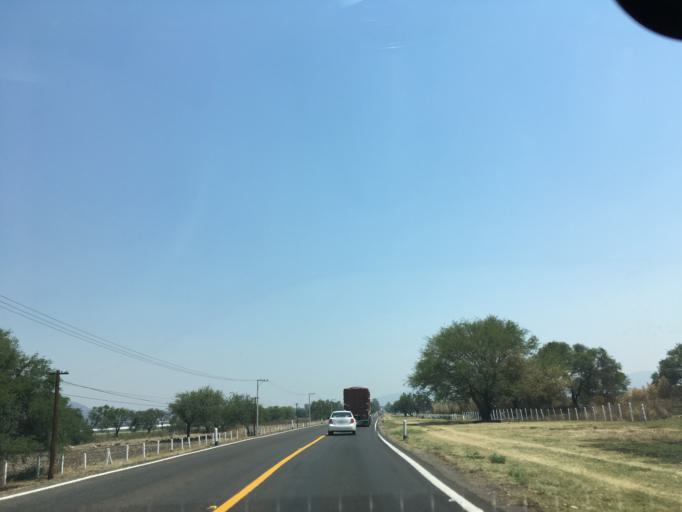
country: MX
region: Michoacan
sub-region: Cuitzeo
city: Cuamio
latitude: 20.0011
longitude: -101.1559
